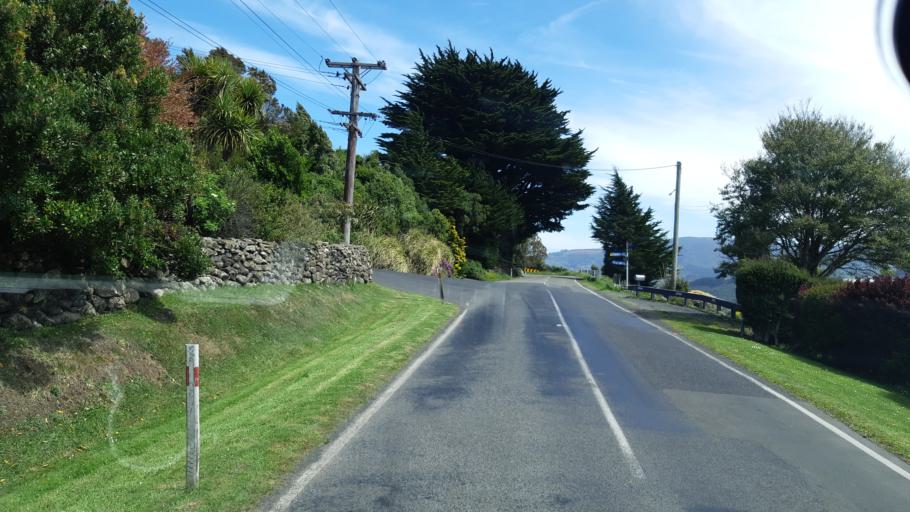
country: NZ
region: Otago
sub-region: Dunedin City
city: Dunedin
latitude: -45.8860
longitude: 170.5713
